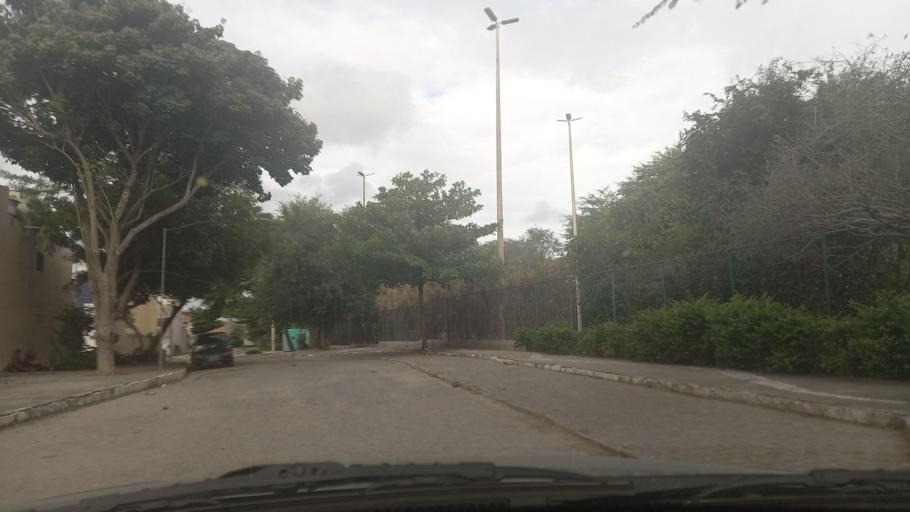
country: BR
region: Pernambuco
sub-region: Caruaru
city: Caruaru
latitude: -8.2930
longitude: -35.9807
